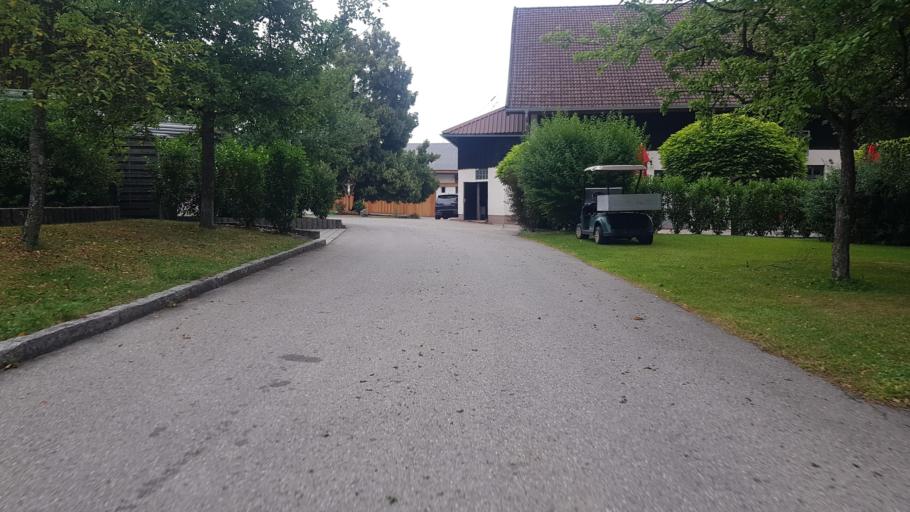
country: DE
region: Bavaria
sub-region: Upper Bavaria
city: Starnberg
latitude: 48.0242
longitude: 11.3488
